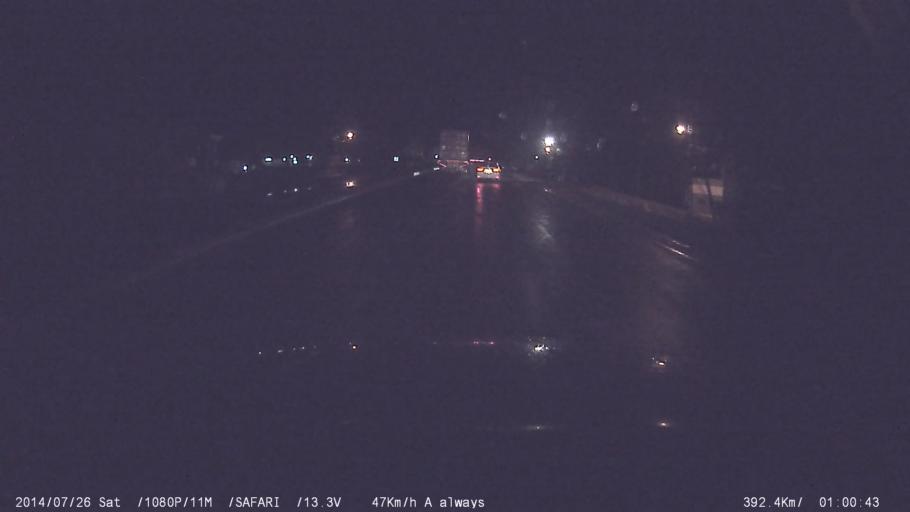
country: IN
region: Kerala
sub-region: Palakkad district
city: Palakkad
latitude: 10.7804
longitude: 76.7132
